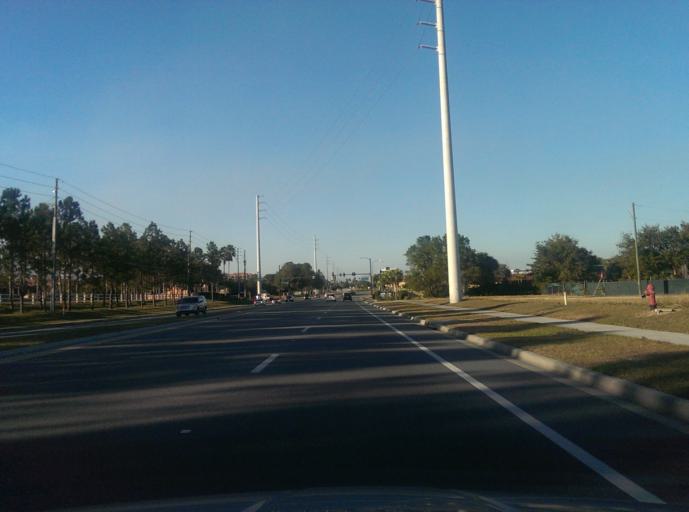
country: US
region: Florida
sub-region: Polk County
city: Citrus Ridge
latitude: 28.3270
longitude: -81.5906
